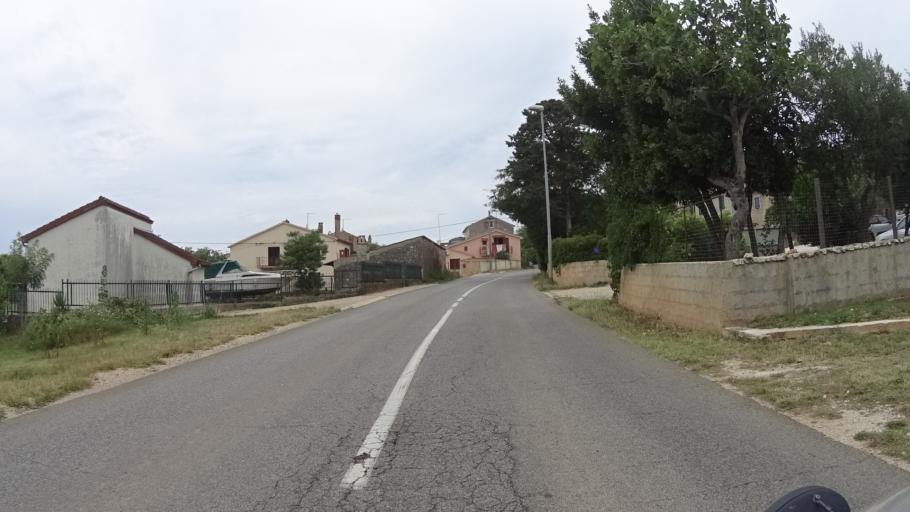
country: HR
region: Istarska
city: Medulin
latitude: 44.8597
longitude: 13.9011
